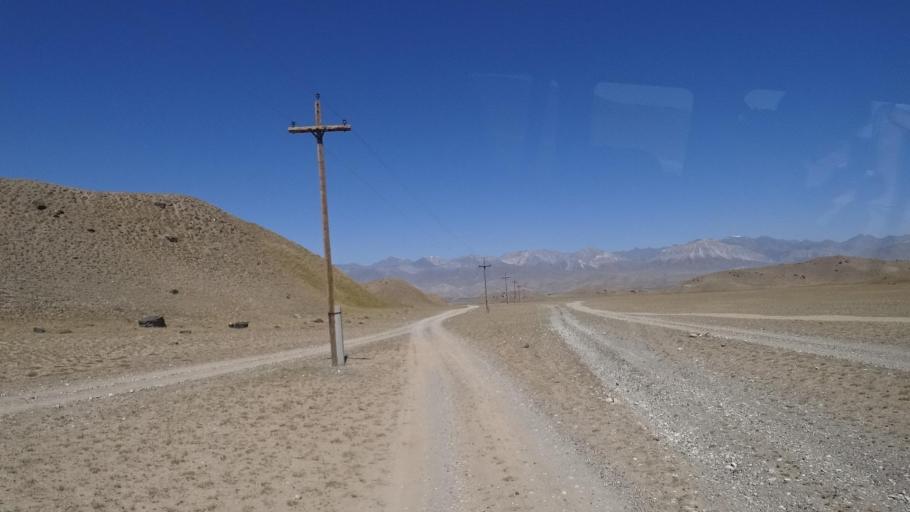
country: KG
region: Osh
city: Gul'cha
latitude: 39.6015
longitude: 72.8813
